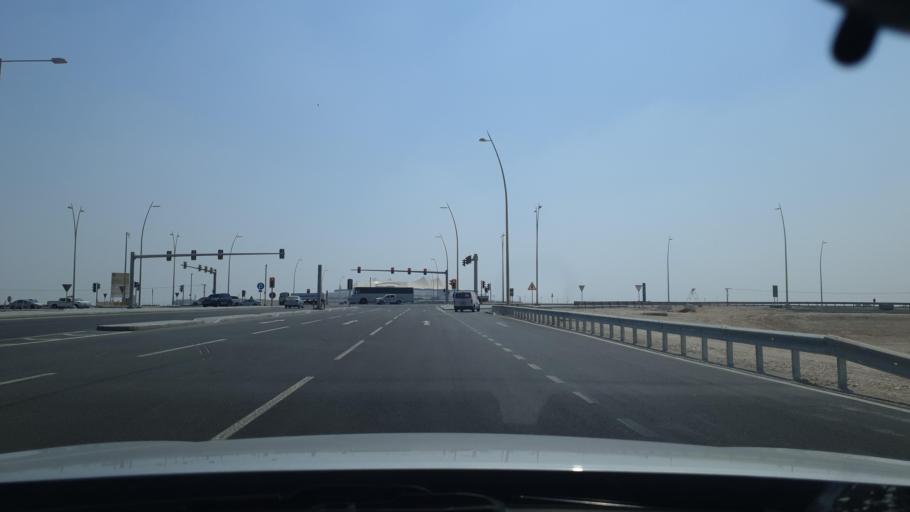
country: QA
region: Al Khawr
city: Al Khawr
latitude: 25.6667
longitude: 51.4749
